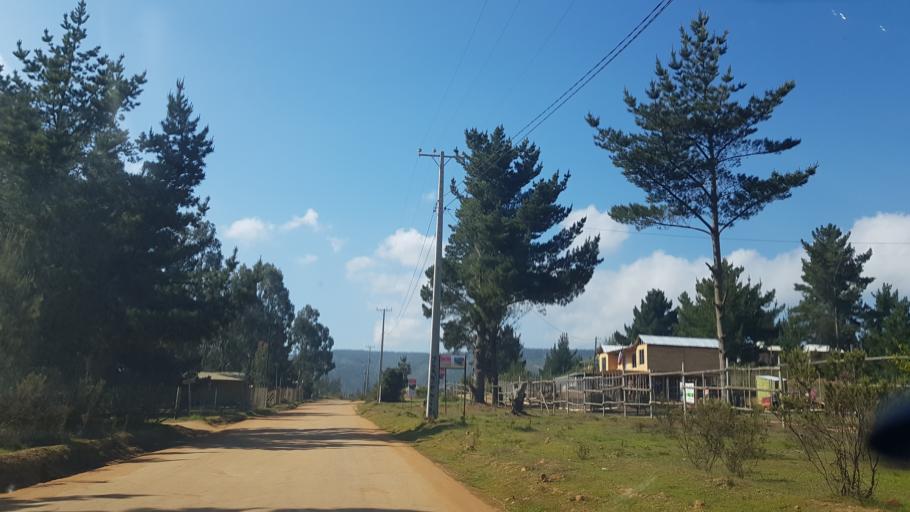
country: CL
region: Valparaiso
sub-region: Provincia de Valparaiso
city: Valparaiso
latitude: -33.1348
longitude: -71.6582
